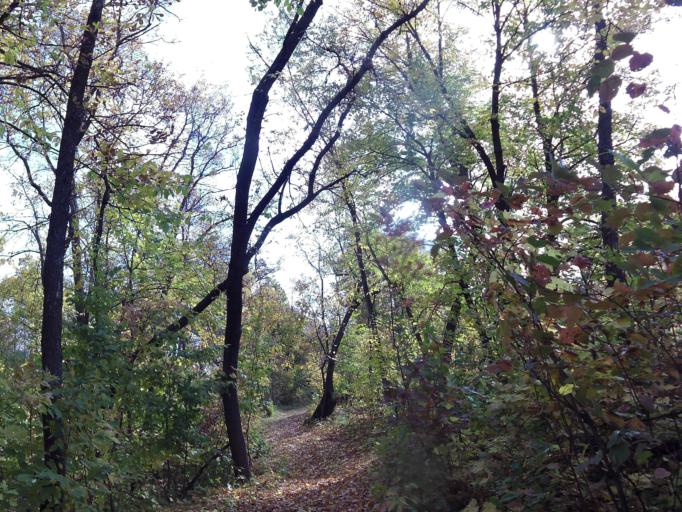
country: US
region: North Dakota
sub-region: Pembina County
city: Cavalier
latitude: 48.7773
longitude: -97.7382
